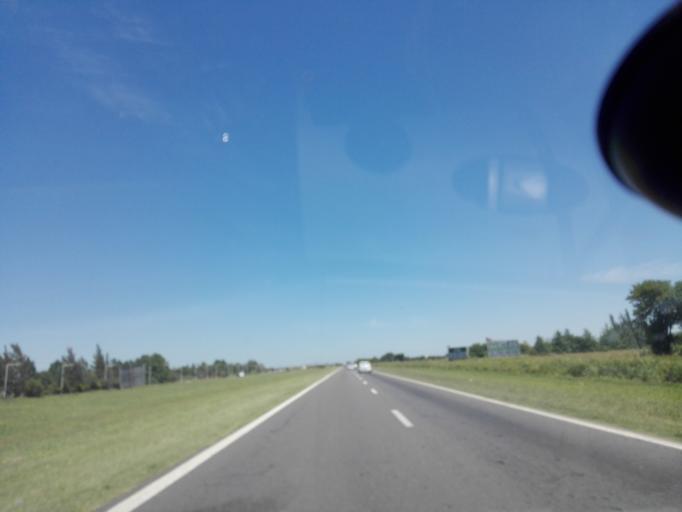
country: AR
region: Santa Fe
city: Roldan
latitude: -32.9289
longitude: -60.8807
